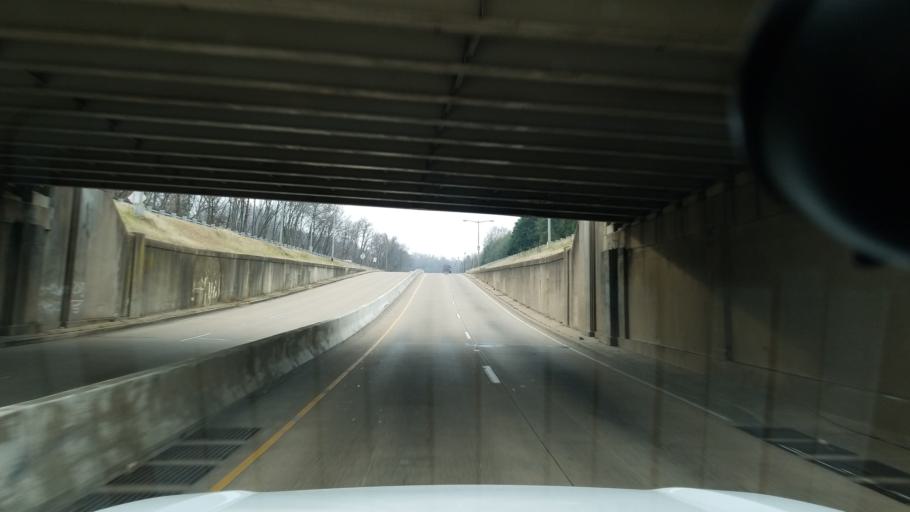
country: US
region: Maryland
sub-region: Prince George's County
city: Glassmanor
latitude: 38.8452
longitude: -77.0084
